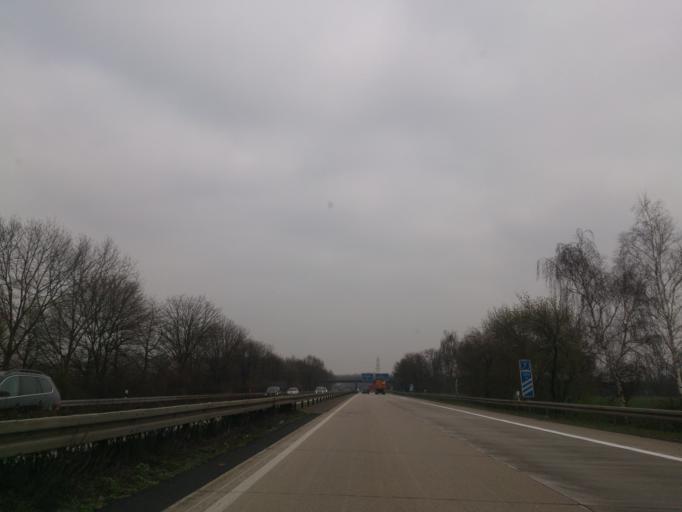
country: DE
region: North Rhine-Westphalia
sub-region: Regierungsbezirk Dusseldorf
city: Viersen
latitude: 51.2105
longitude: 6.3634
